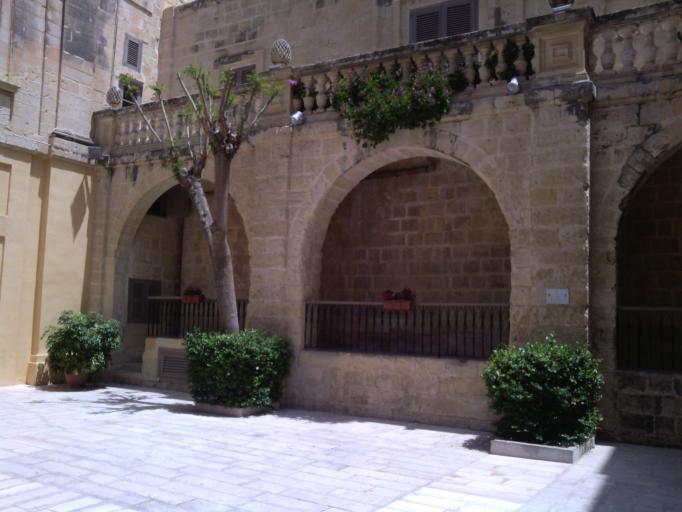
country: MT
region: L-Imdina
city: Imdina
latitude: 35.8851
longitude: 14.4042
